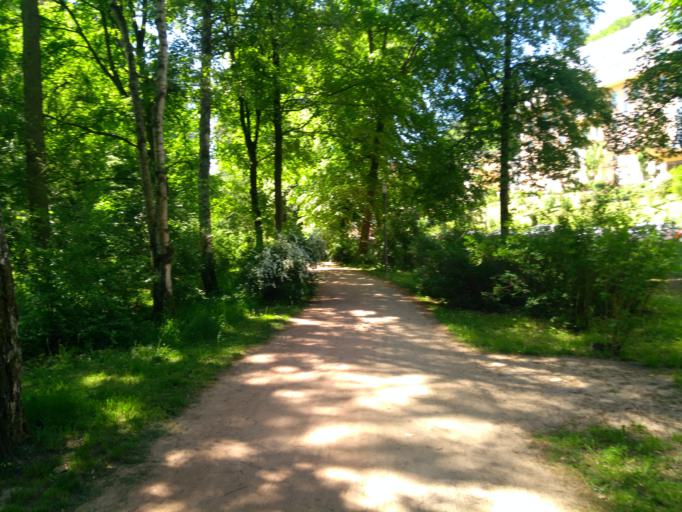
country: DE
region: Bavaria
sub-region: Regierungsbezirk Unterfranken
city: Bad Kissingen
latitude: 50.1958
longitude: 10.0732
